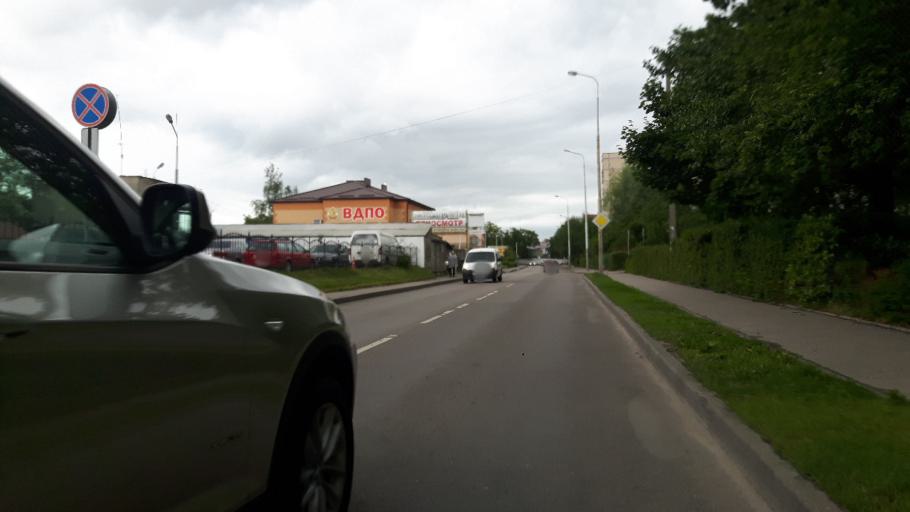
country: RU
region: Kaliningrad
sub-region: Gorod Kaliningrad
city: Kaliningrad
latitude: 54.7352
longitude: 20.5015
